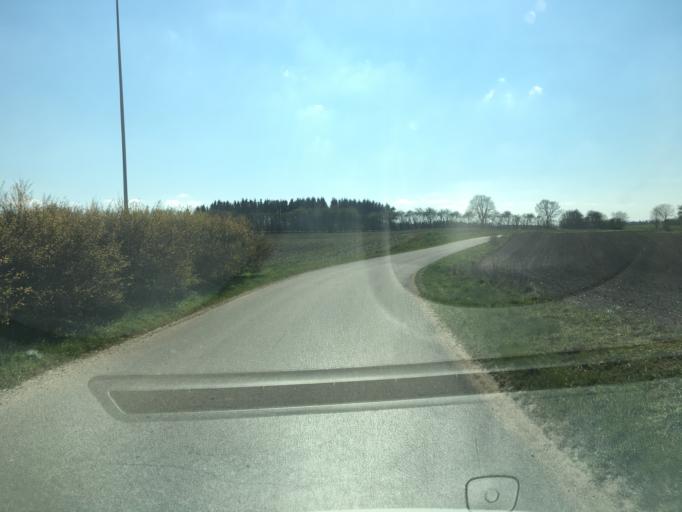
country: DK
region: South Denmark
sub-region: Aabenraa Kommune
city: Krusa
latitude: 54.9243
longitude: 9.4775
